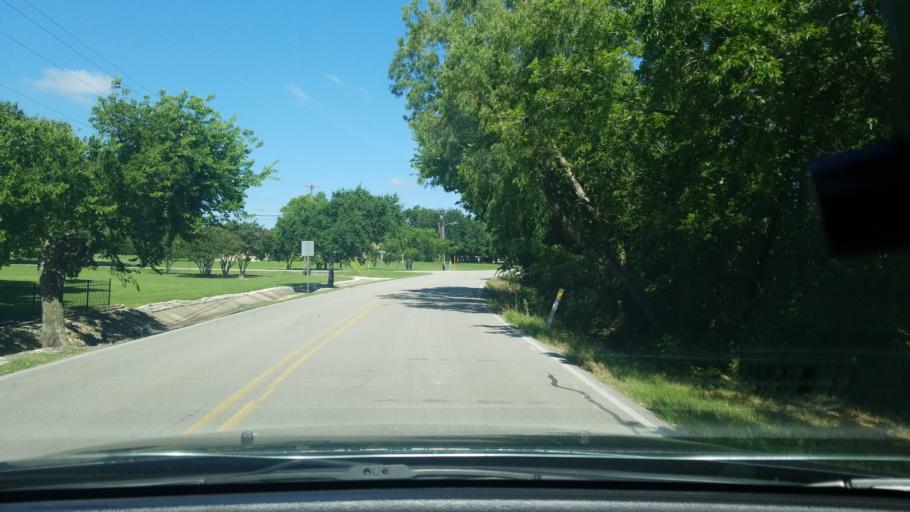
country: US
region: Texas
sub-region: Dallas County
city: Sunnyvale
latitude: 32.7937
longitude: -96.5539
